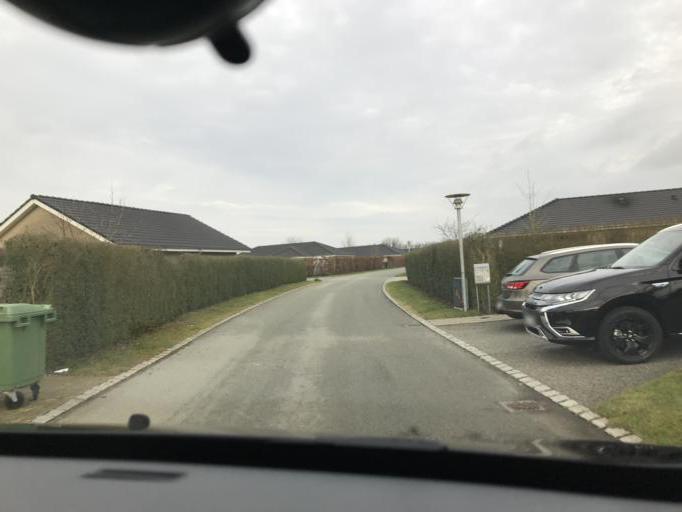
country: DK
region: South Denmark
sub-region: Faaborg-Midtfyn Kommune
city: Ringe
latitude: 55.2474
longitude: 10.4691
